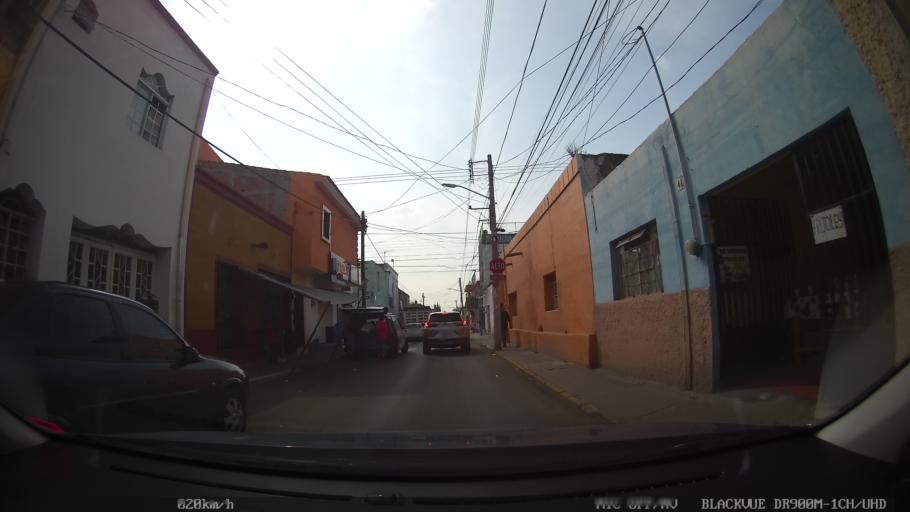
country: MX
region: Jalisco
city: Tonala
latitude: 20.6223
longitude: -103.2410
